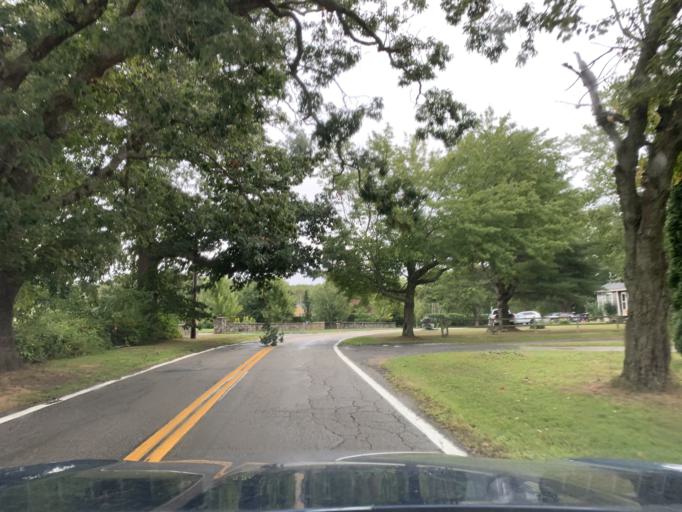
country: US
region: Rhode Island
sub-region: Bristol County
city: Warren
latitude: 41.7544
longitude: -71.2687
